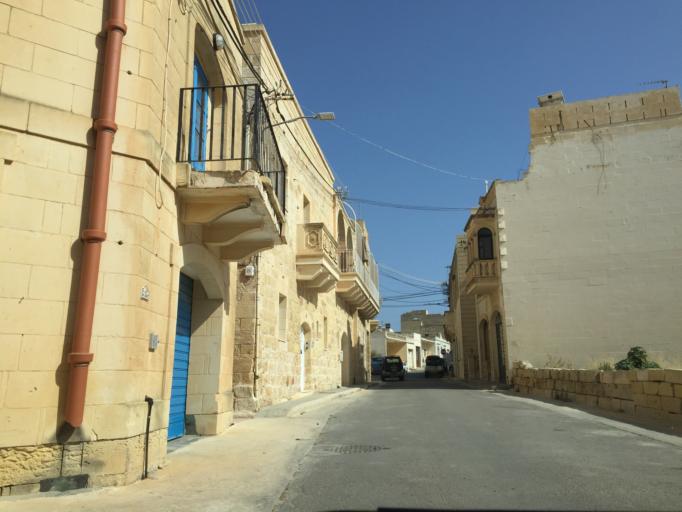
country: MT
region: L-Gharb
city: Gharb
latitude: 36.0634
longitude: 14.2070
